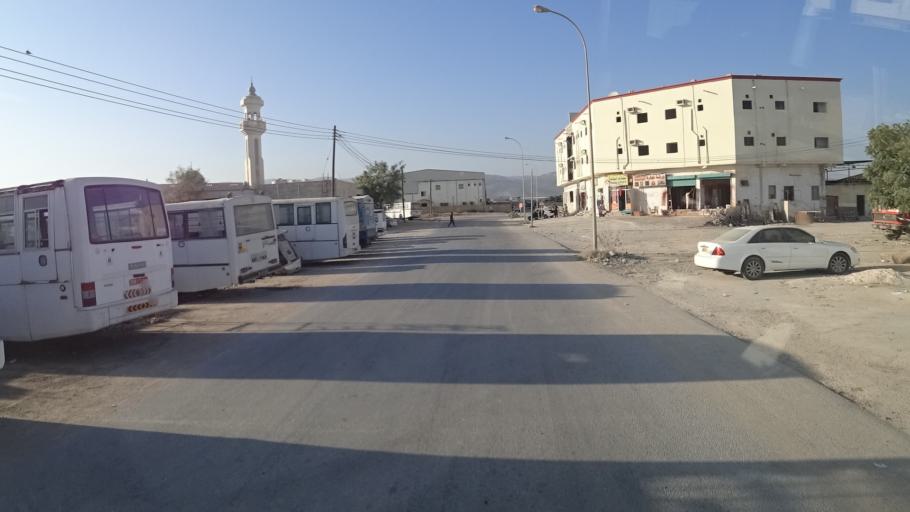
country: OM
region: Zufar
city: Salalah
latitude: 17.0236
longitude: 54.0451
